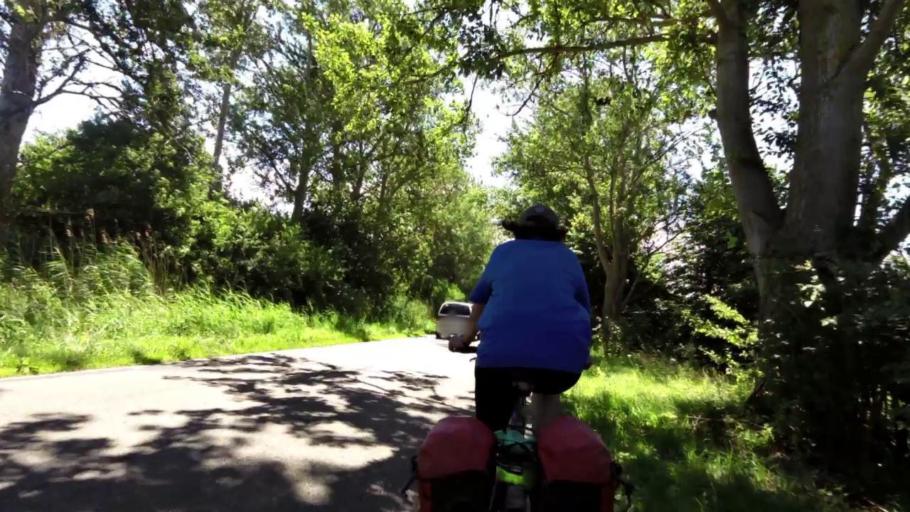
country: PL
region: West Pomeranian Voivodeship
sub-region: Koszalin
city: Koszalin
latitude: 54.2893
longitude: 16.2103
